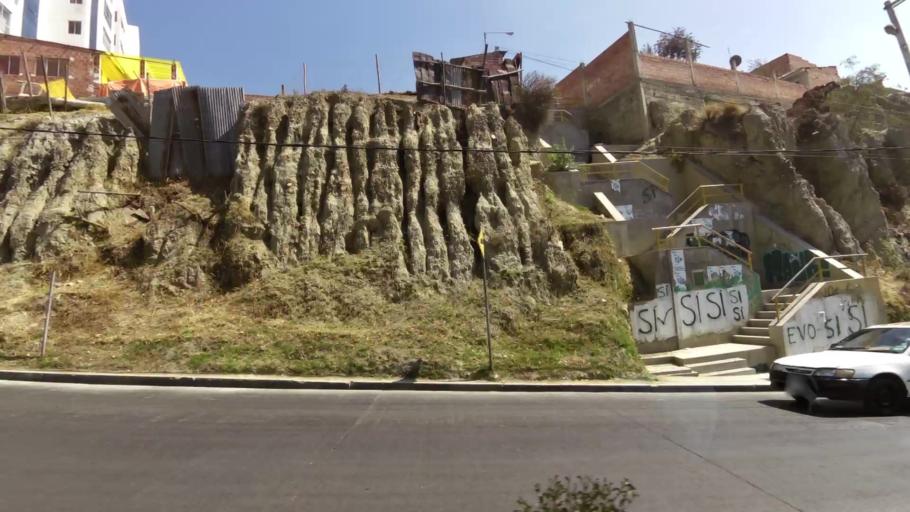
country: BO
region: La Paz
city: La Paz
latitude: -16.5259
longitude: -68.1237
